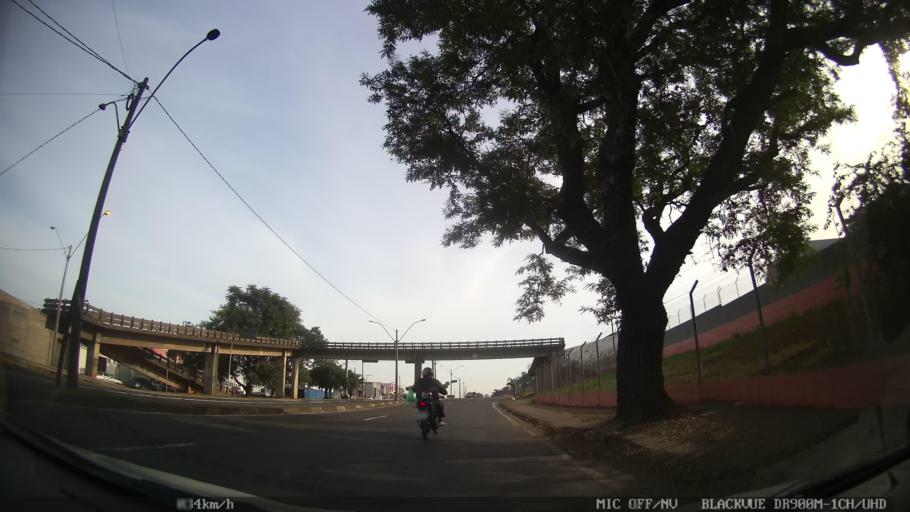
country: BR
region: Sao Paulo
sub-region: Piracicaba
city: Piracicaba
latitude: -22.7007
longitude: -47.6584
